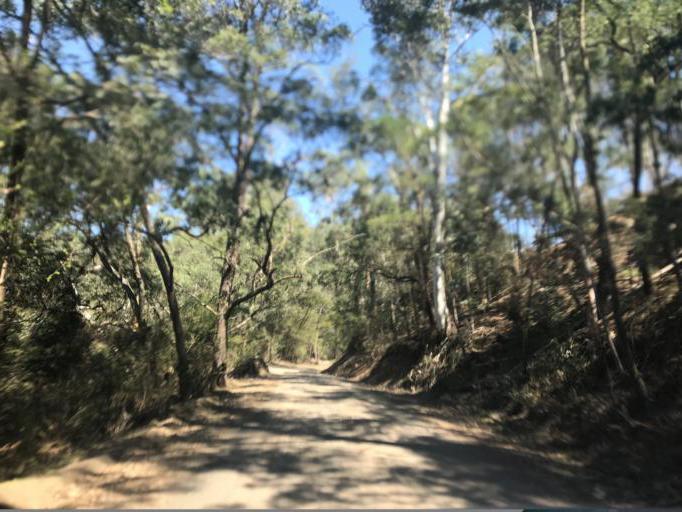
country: AU
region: New South Wales
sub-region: Wyong Shire
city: Little Jilliby
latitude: -33.1979
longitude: 151.0232
